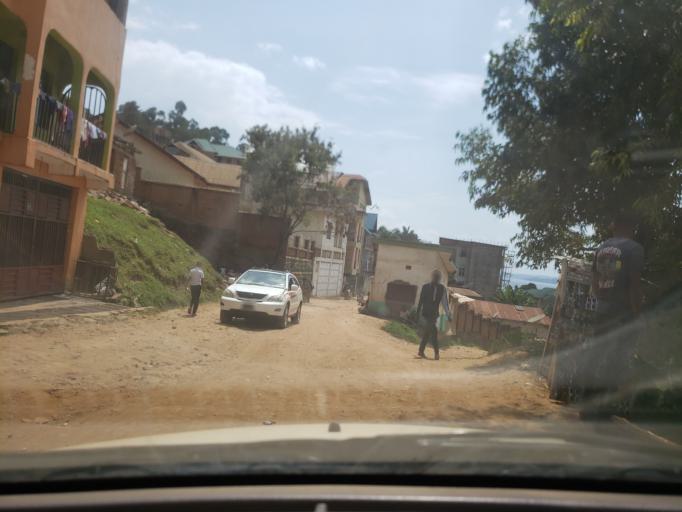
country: CD
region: South Kivu
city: Bukavu
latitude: -2.4991
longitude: 28.8615
